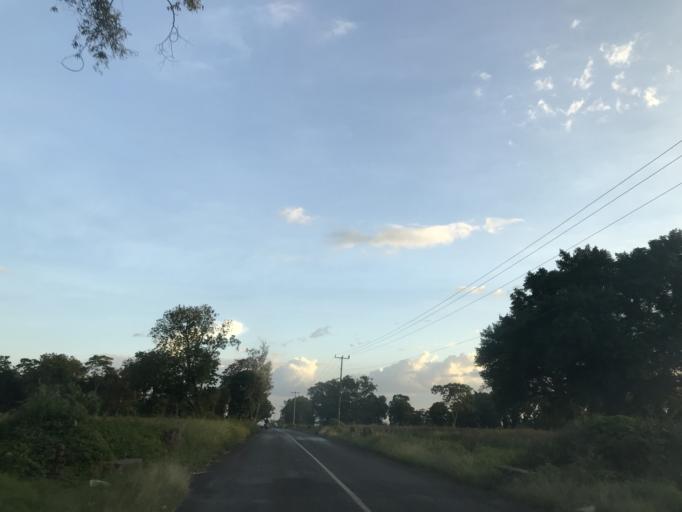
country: TZ
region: Arusha
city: Usa River
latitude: -3.3578
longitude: 36.8662
